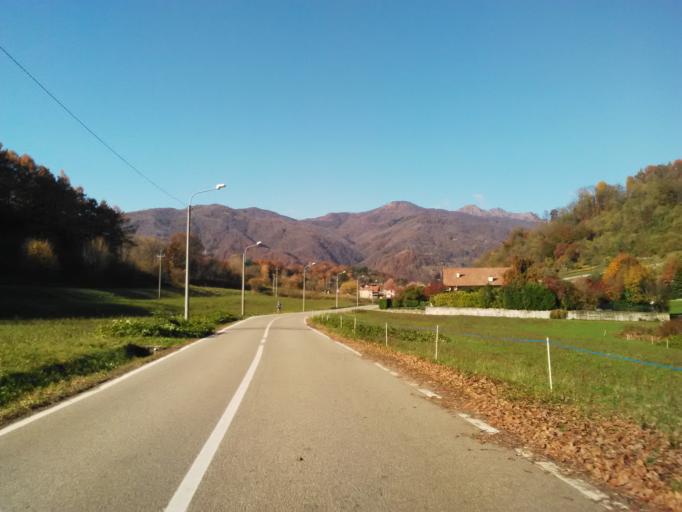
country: IT
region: Piedmont
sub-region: Provincia di Vercelli
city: Borgosesia
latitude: 45.7333
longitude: 8.2800
